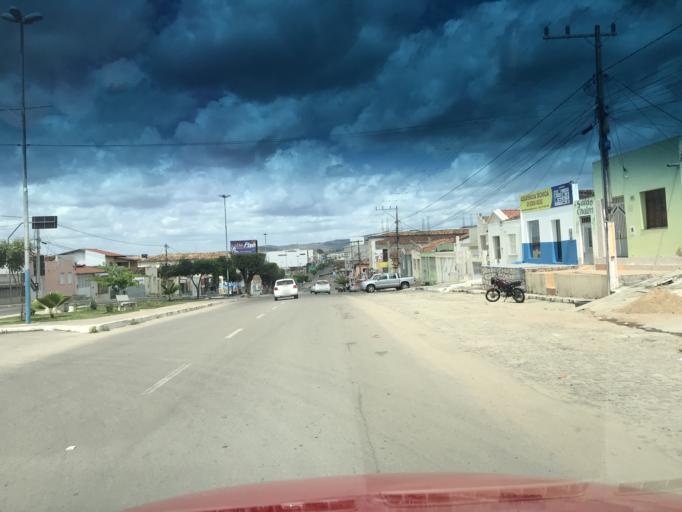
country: BR
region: Bahia
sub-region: Itaberaba
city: Itaberaba
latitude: -12.5262
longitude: -40.3068
